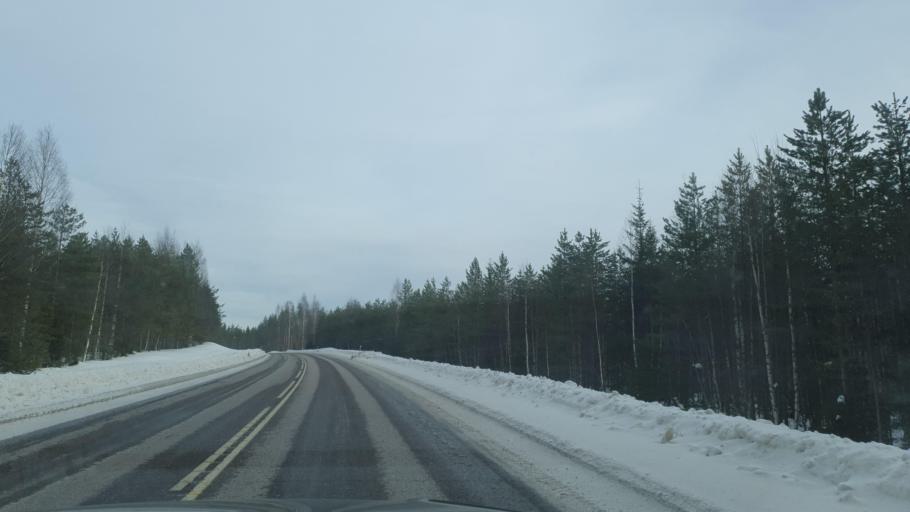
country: FI
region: Kainuu
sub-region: Kajaani
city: Vuolijoki
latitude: 64.4840
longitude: 27.3448
